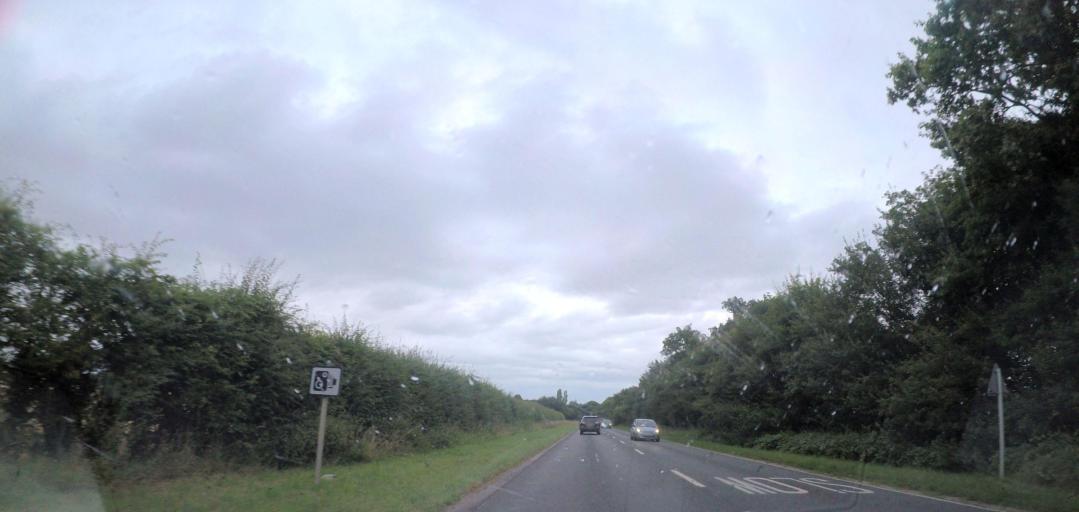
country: GB
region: England
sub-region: Norfolk
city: Coltishall
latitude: 52.7129
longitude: 1.3498
